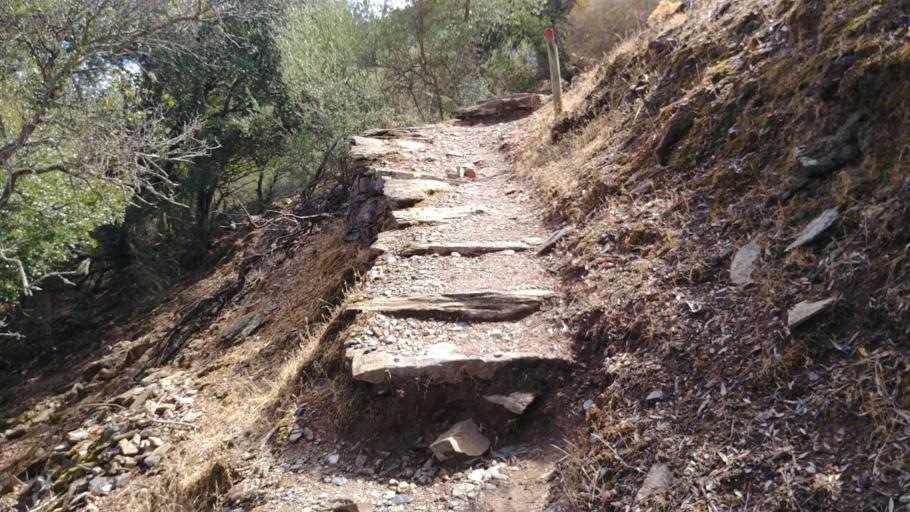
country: ES
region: Extremadura
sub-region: Provincia de Caceres
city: Torrejon el Rubio
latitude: 39.8303
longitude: -6.0373
